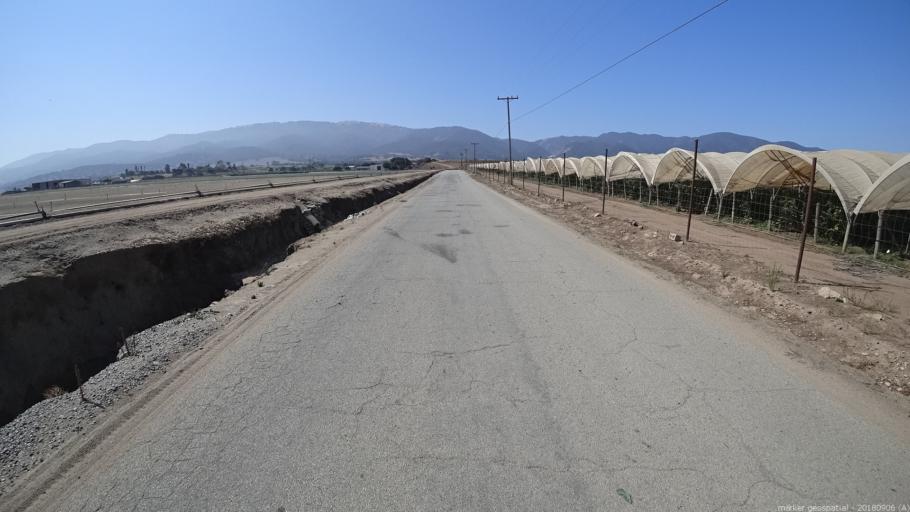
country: US
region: California
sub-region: Monterey County
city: Chualar
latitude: 36.5919
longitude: -121.6039
